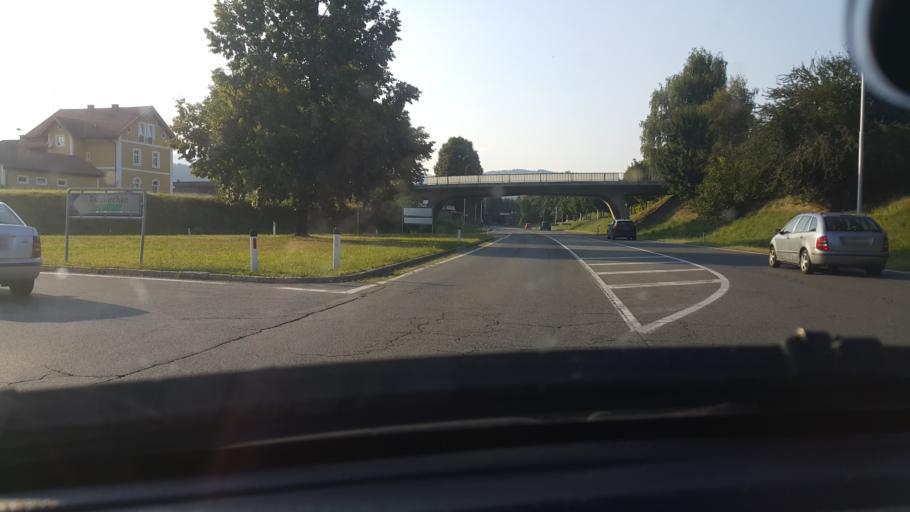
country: AT
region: Carinthia
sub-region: Politischer Bezirk Feldkirchen
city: Feldkirchen in Karnten
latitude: 46.7241
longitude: 14.1045
